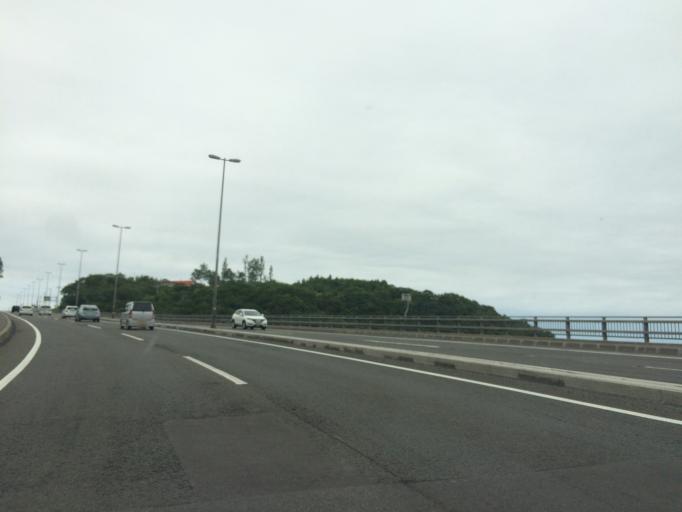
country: JP
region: Hokkaido
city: Otaru
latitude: 43.1576
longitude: 141.1123
